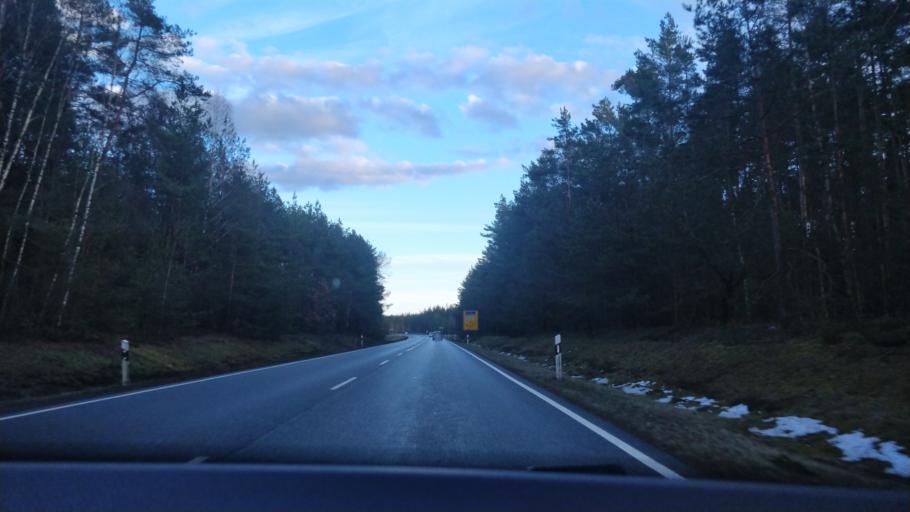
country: DE
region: Bavaria
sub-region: Upper Palatinate
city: Schwarzenbach
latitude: 49.7276
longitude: 11.9638
